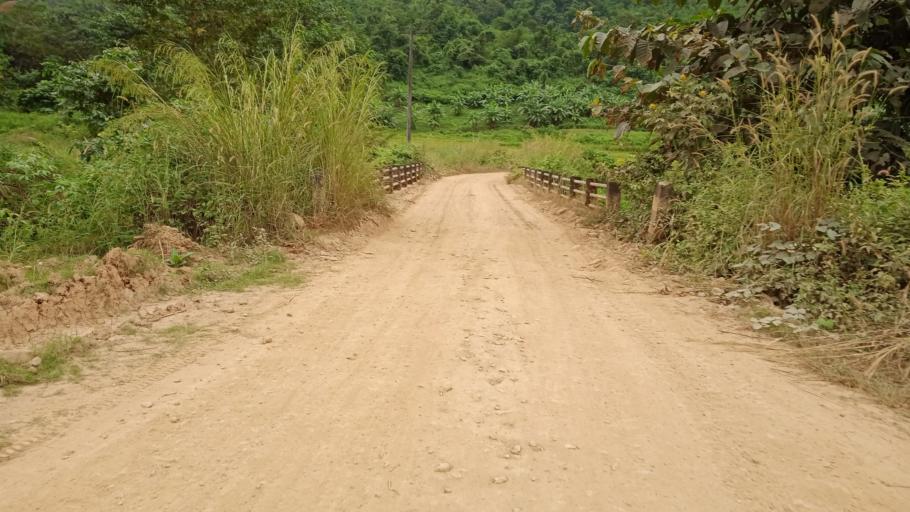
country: LA
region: Xiangkhoang
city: Phonsavan
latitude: 19.0926
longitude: 102.9952
